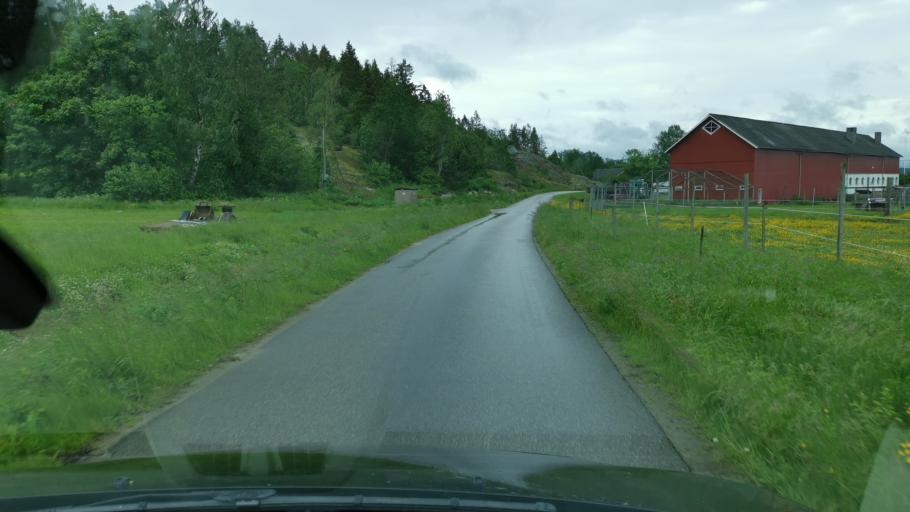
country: SE
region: Vaestra Goetaland
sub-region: Orust
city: Henan
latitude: 58.3235
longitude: 11.7185
